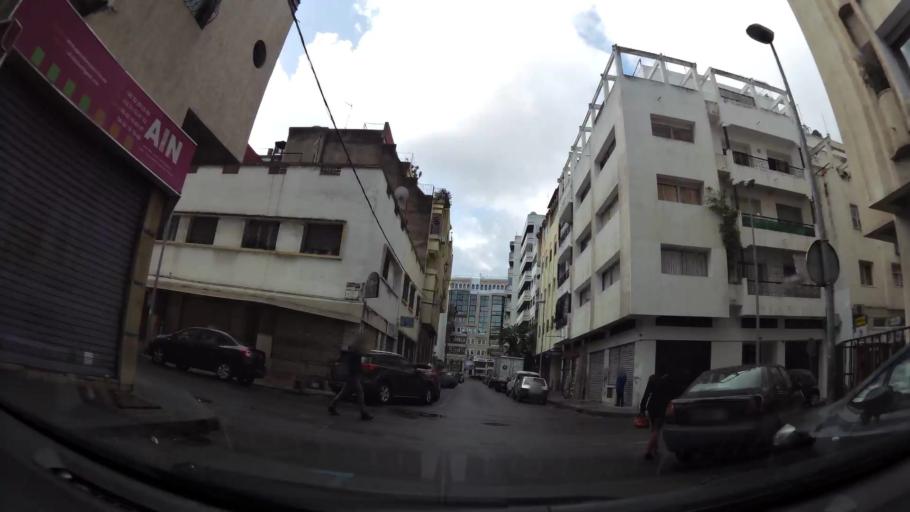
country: MA
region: Grand Casablanca
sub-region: Casablanca
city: Casablanca
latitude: 33.5839
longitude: -7.6169
